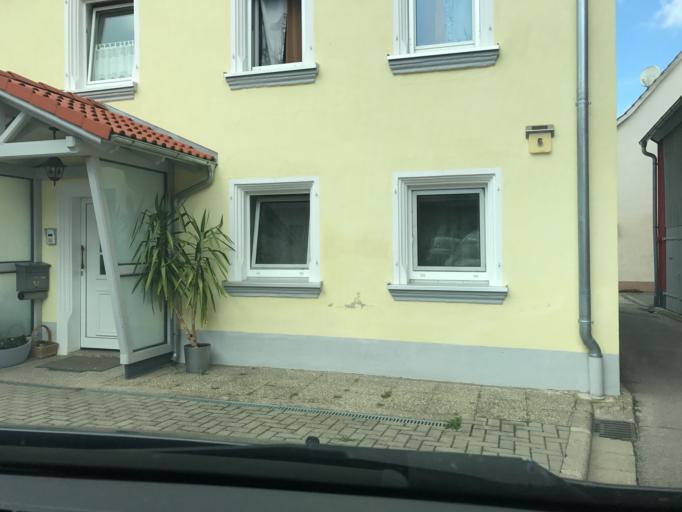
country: DE
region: Bavaria
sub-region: Regierungsbezirk Mittelfranken
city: Wittelshofen
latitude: 49.0610
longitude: 10.4801
